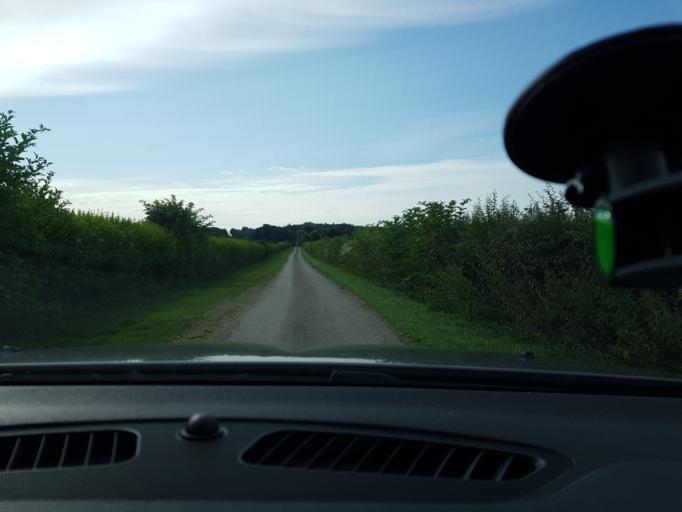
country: GB
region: England
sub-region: West Berkshire
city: Hungerford
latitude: 51.4019
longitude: -1.4843
